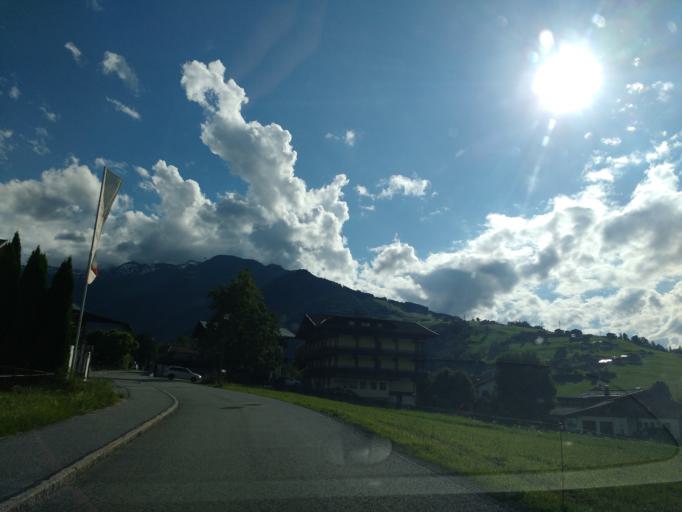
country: AT
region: Salzburg
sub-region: Politischer Bezirk Zell am See
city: Kaprun
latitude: 47.2721
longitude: 12.7634
